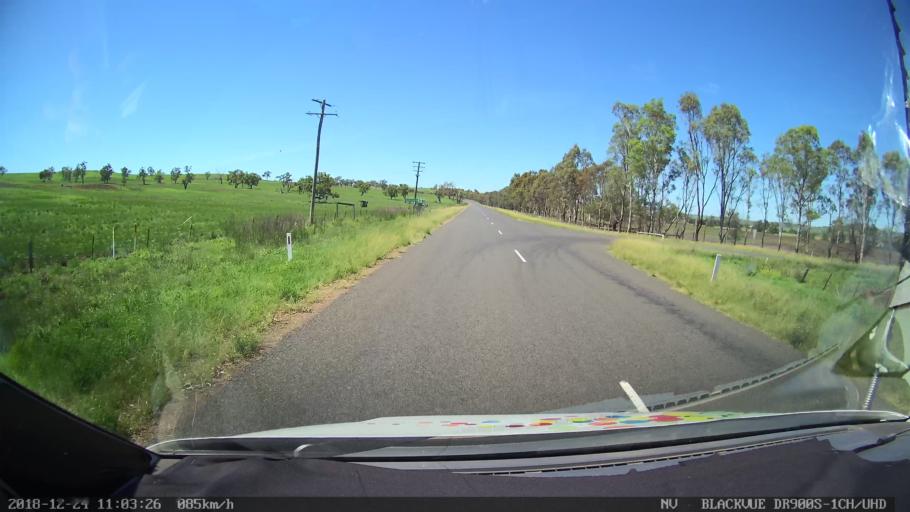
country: AU
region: New South Wales
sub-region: Upper Hunter Shire
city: Merriwa
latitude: -32.0967
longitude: 150.3688
